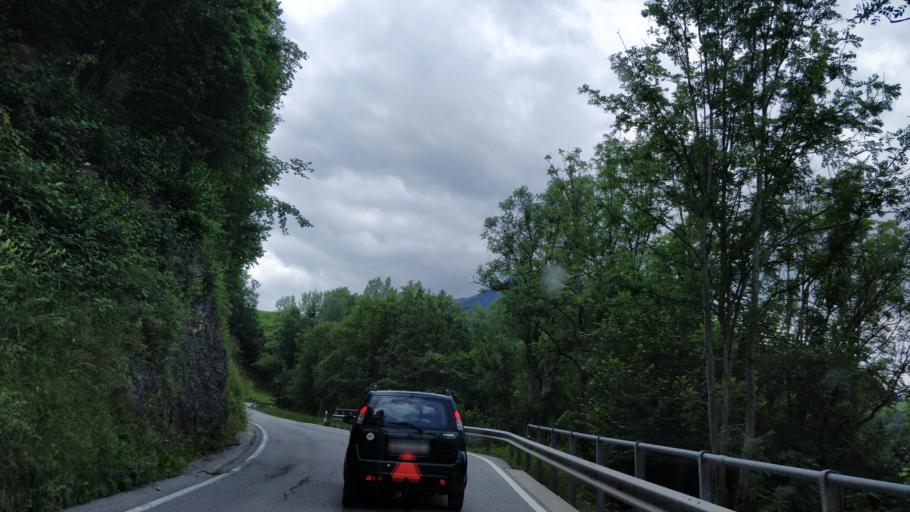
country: CH
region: Grisons
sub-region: Surselva District
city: Ilanz
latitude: 46.6953
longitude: 9.1836
